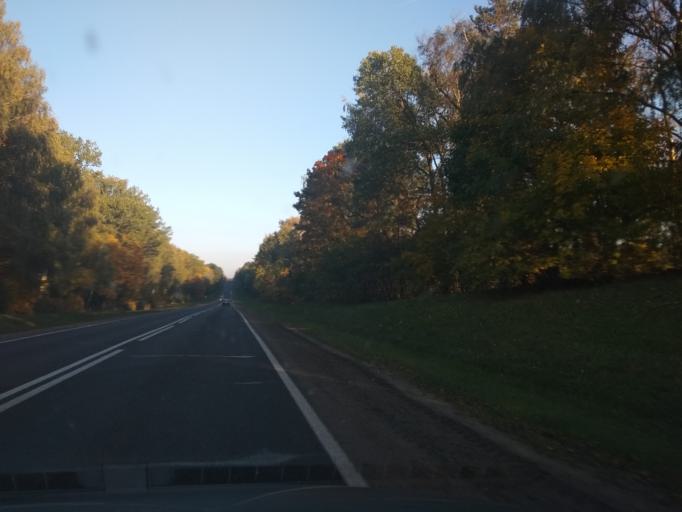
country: BY
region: Grodnenskaya
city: Vawkavysk
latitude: 53.1488
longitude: 24.5751
